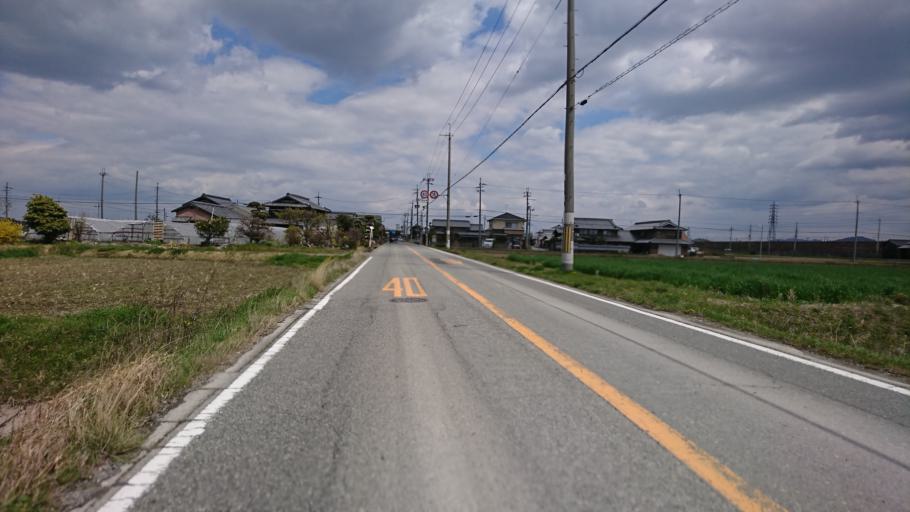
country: JP
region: Hyogo
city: Miki
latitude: 34.7503
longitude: 134.9392
